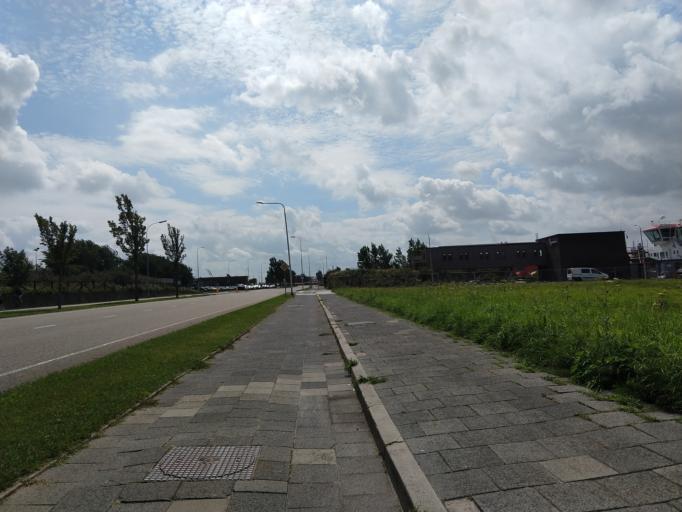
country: NL
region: Zeeland
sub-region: Gemeente Vlissingen
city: Vlissingen
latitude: 51.4468
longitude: 3.5940
